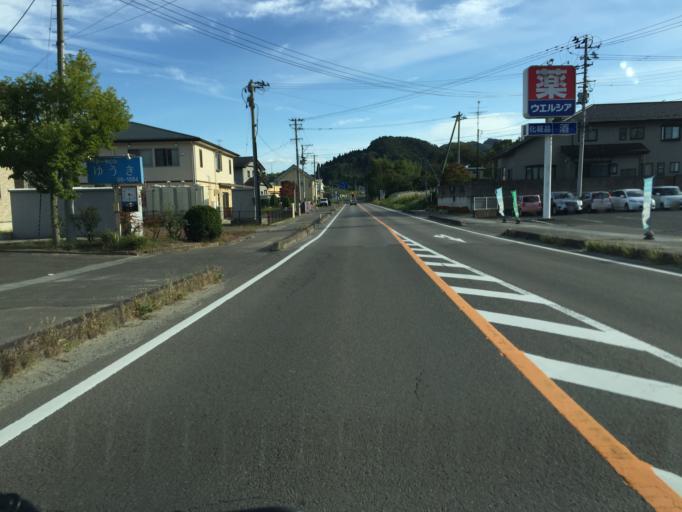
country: JP
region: Fukushima
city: Hobaramachi
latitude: 37.7843
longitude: 140.5899
